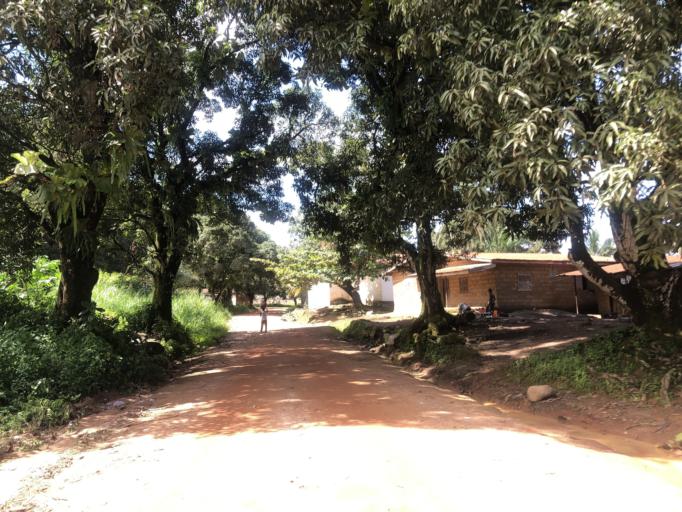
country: SL
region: Eastern Province
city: Koidu
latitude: 8.6375
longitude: -10.9694
